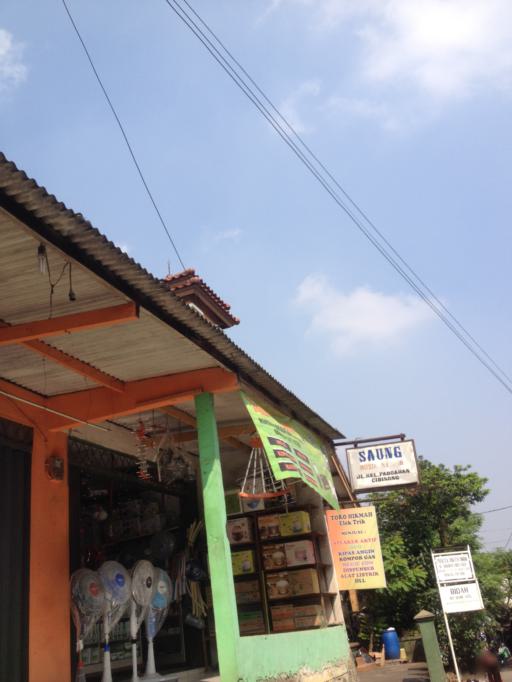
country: ID
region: West Java
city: Cibinong
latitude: -6.4653
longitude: 106.8527
